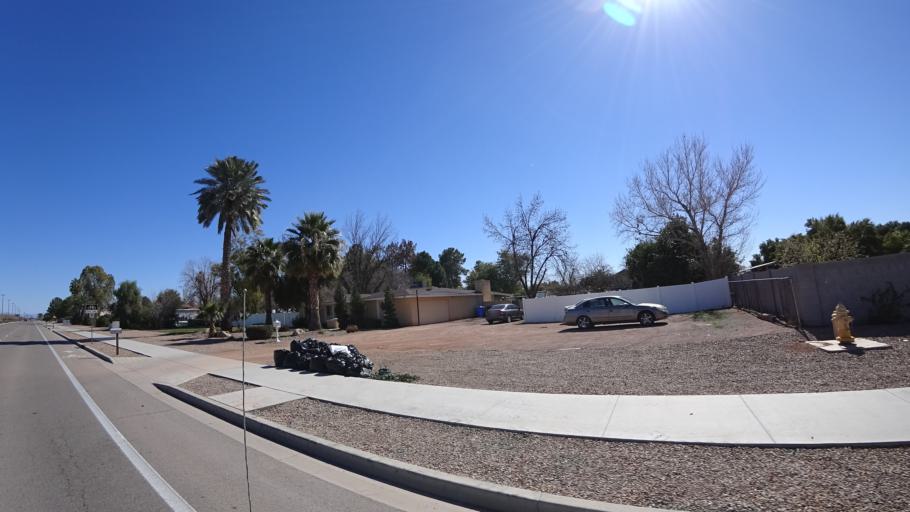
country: US
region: Arizona
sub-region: Maricopa County
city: Gilbert
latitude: 33.3064
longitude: -111.7801
